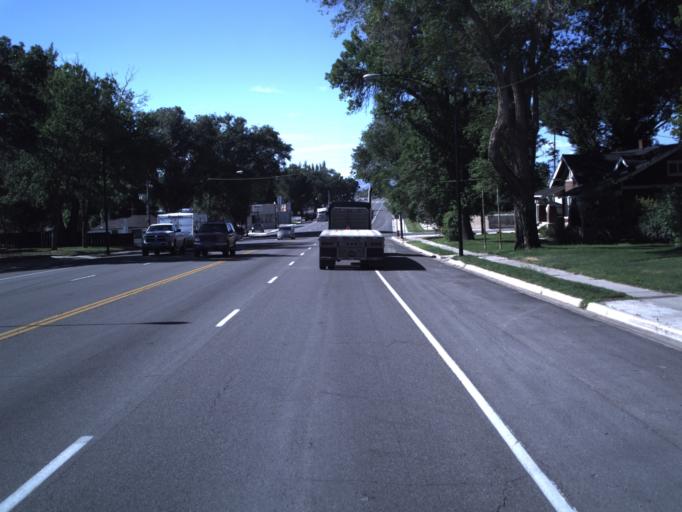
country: US
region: Utah
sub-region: Sanpete County
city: Gunnison
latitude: 39.1520
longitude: -111.8184
